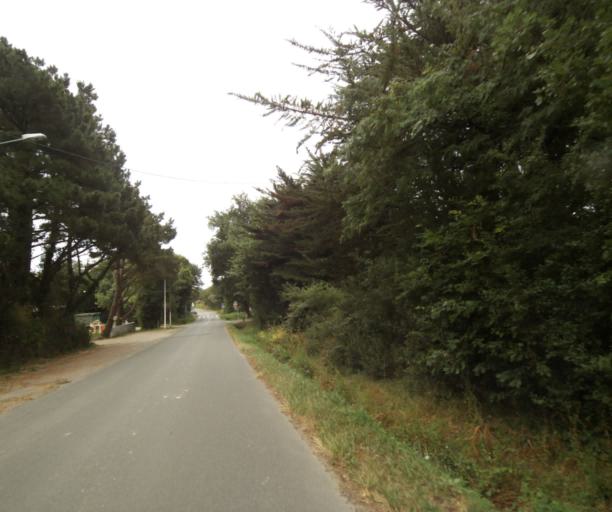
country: FR
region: Pays de la Loire
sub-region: Departement de la Vendee
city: Chateau-d'Olonne
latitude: 46.4826
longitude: -1.7274
